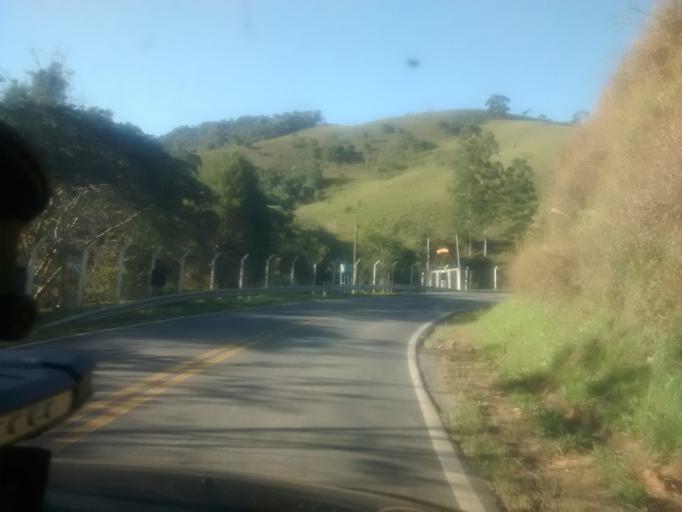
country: BR
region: Sao Paulo
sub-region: Campos Do Jordao
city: Campos do Jordao
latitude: -22.8232
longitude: -45.7316
